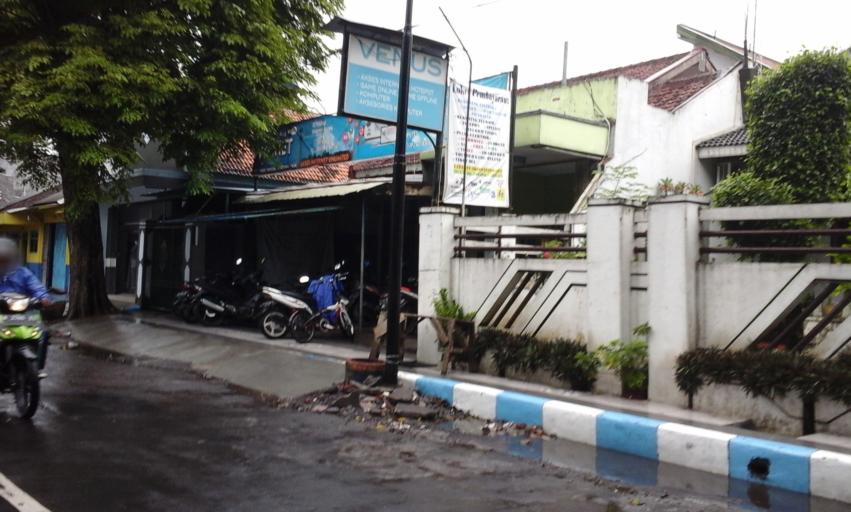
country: ID
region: East Java
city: Kadipaten
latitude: -8.1302
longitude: 113.2172
